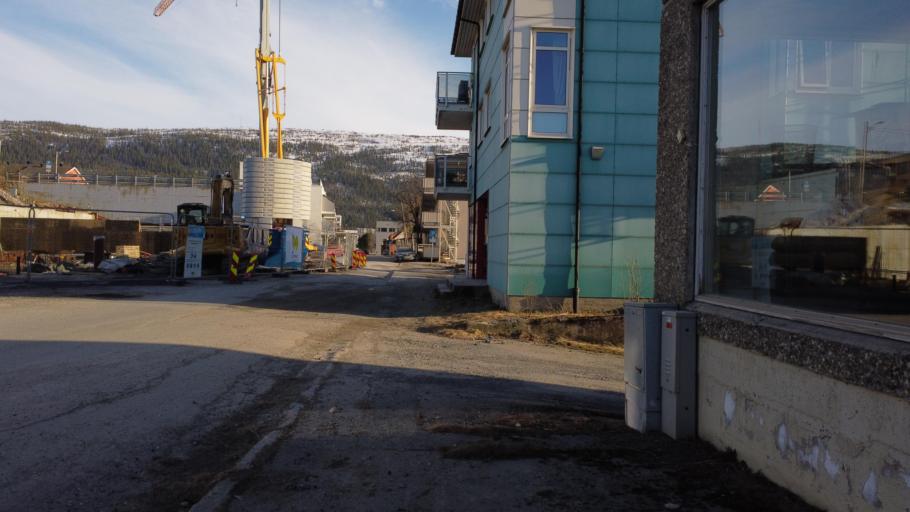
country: NO
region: Nordland
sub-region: Rana
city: Mo i Rana
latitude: 66.3154
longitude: 14.1317
